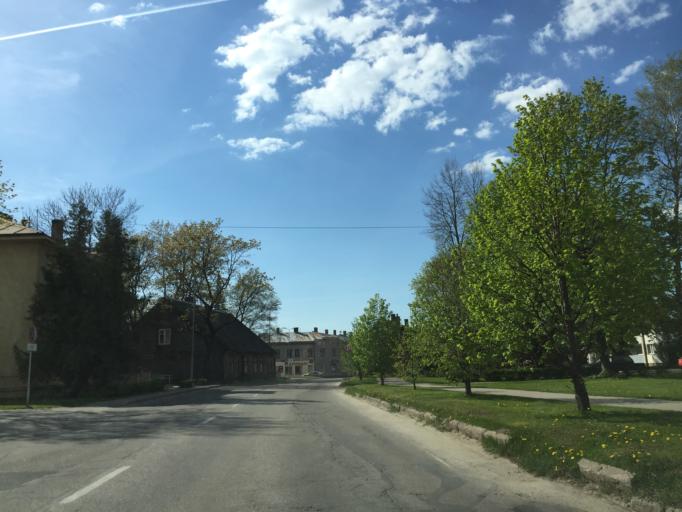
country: LV
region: Limbazu Rajons
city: Limbazi
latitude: 57.5130
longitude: 24.7186
